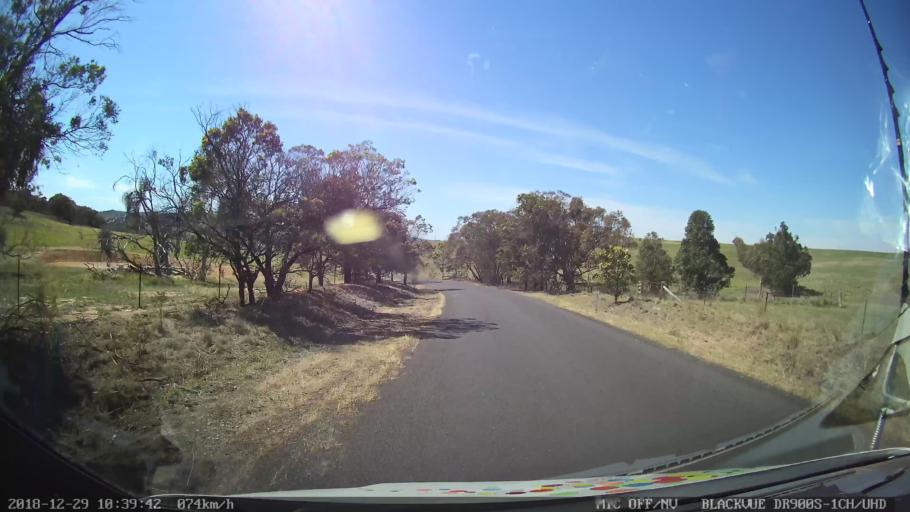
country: AU
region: New South Wales
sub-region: Palerang
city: Bungendore
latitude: -35.0092
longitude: 149.5116
